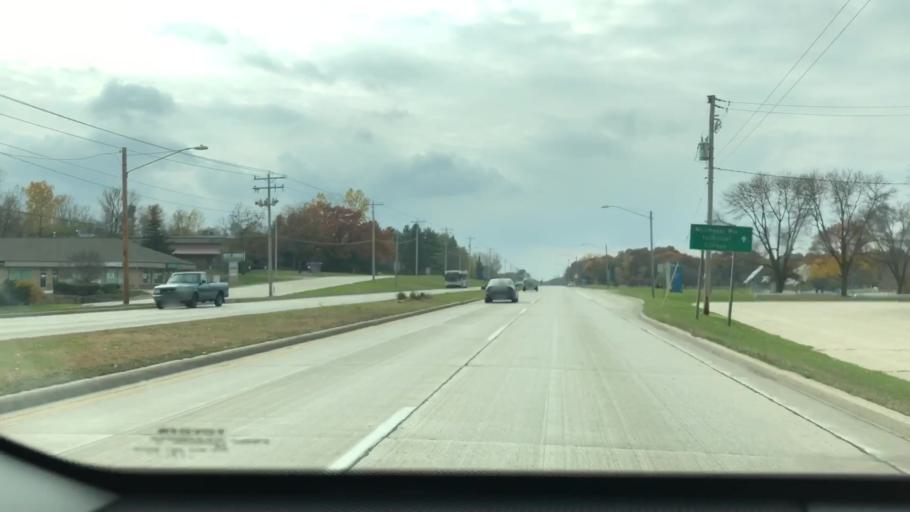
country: US
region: Wisconsin
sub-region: Brown County
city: Howard
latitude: 44.5240
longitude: -88.1024
